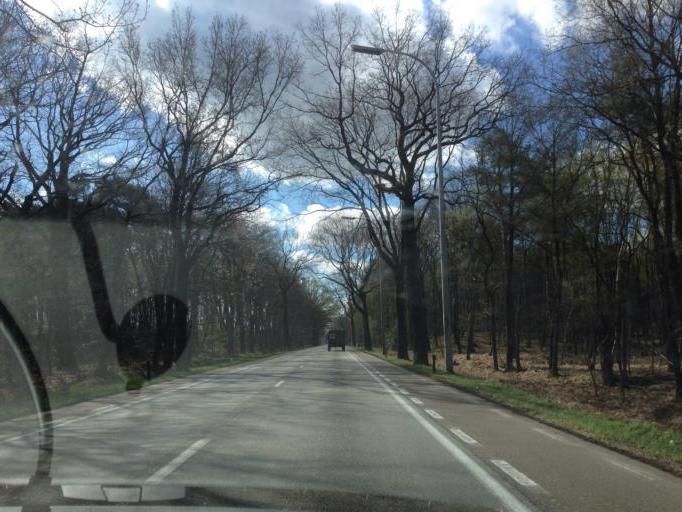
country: BE
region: Flanders
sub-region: Provincie Limburg
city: Helchteren
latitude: 51.0864
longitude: 5.3774
